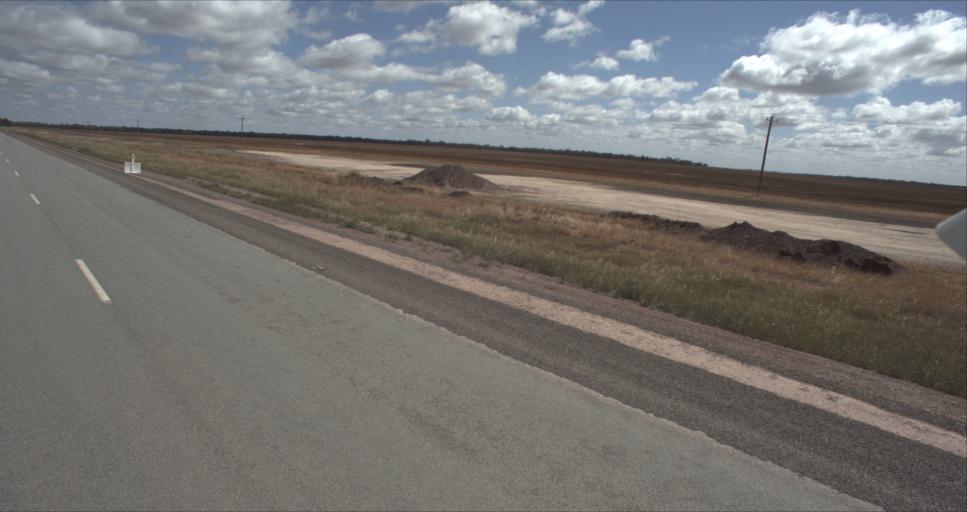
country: AU
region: New South Wales
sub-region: Murrumbidgee Shire
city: Darlington Point
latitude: -34.5704
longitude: 146.0355
